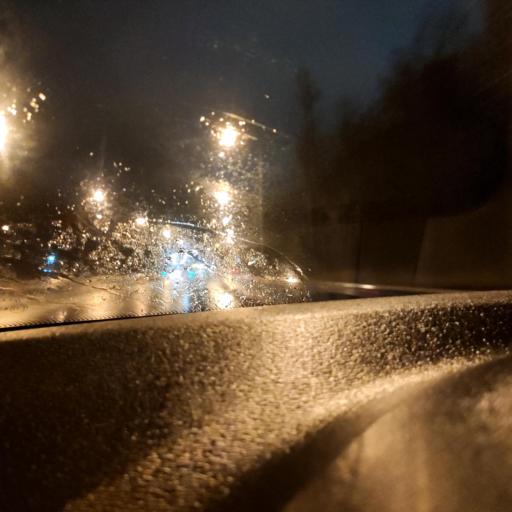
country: RU
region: Samara
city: Petra-Dubrava
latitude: 53.2835
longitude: 50.2515
